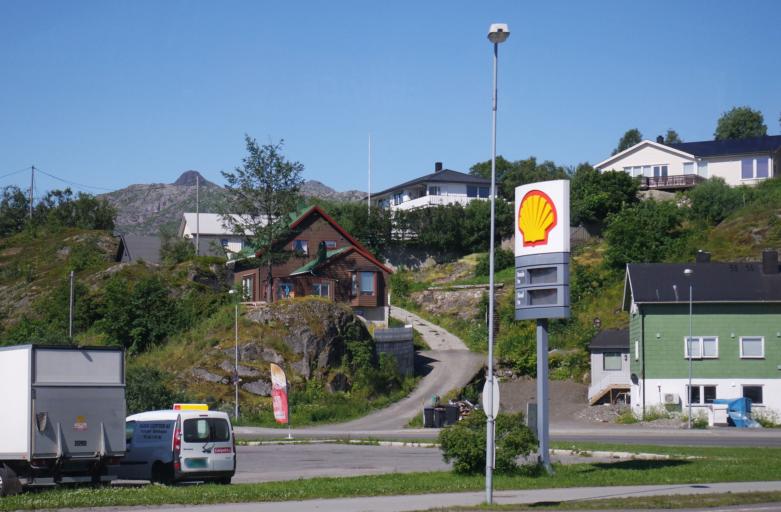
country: NO
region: Nordland
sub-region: Vagan
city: Svolvaer
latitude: 68.2390
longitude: 14.5675
